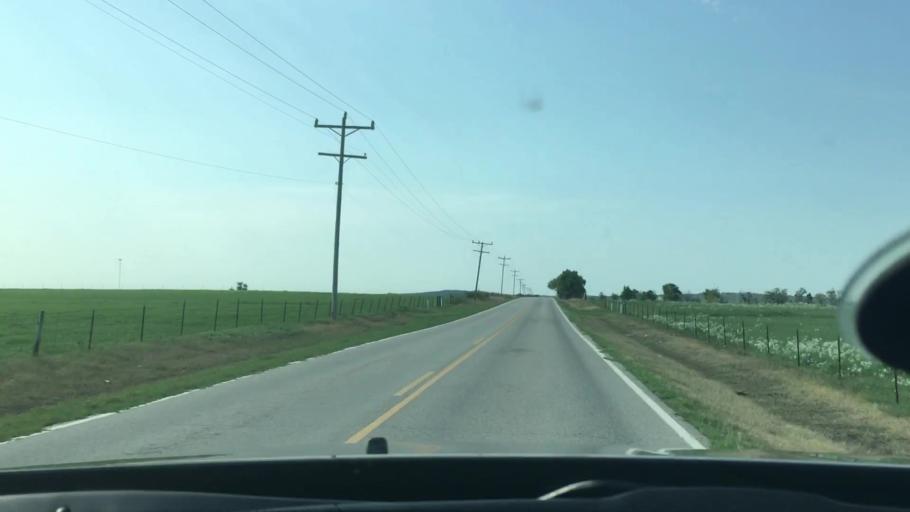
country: US
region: Oklahoma
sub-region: Bryan County
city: Durant
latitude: 34.1120
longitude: -96.4877
